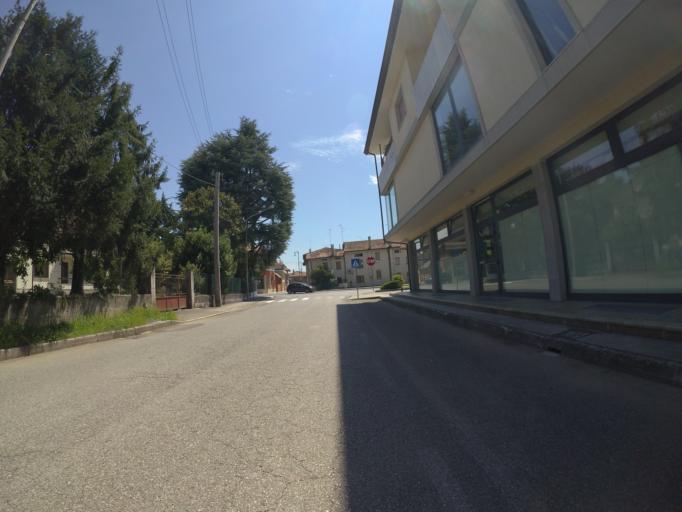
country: IT
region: Friuli Venezia Giulia
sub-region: Provincia di Udine
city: Talmassons
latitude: 45.9308
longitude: 13.1180
